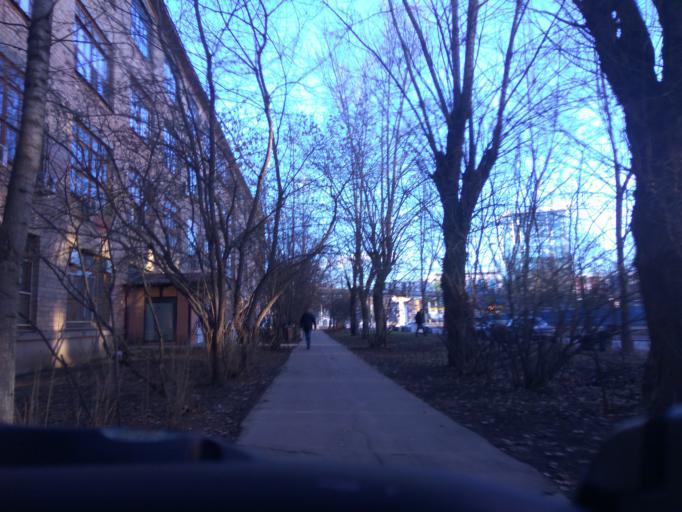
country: RU
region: Moscow
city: Ostankinskiy
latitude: 55.8200
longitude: 37.6030
